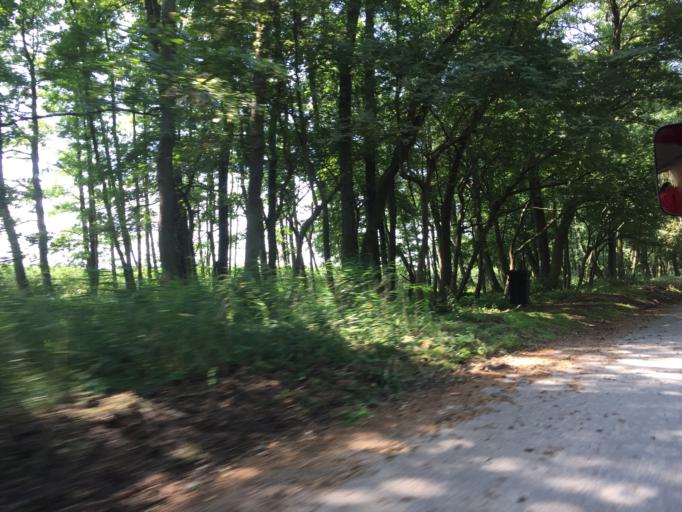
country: PL
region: Pomeranian Voivodeship
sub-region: Powiat leborski
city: Leba
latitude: 54.7523
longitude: 17.4784
